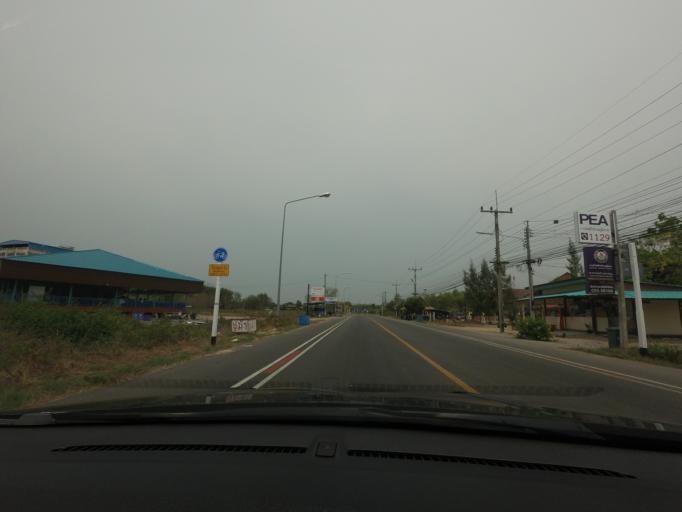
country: TH
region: Phetchaburi
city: Ban Laem
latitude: 13.2746
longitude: 99.9297
